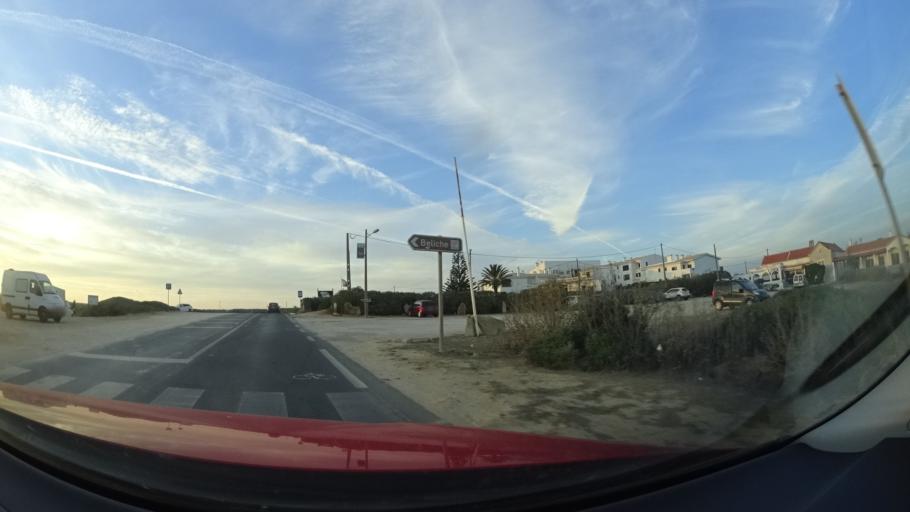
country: PT
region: Faro
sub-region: Vila do Bispo
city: Sagres
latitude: 37.0260
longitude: -8.9628
